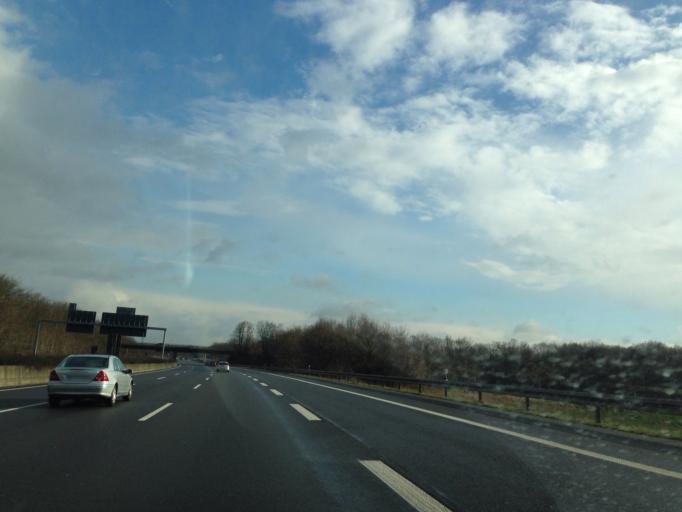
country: DE
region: North Rhine-Westphalia
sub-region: Regierungsbezirk Dusseldorf
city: Meerbusch
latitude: 51.2829
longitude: 6.6366
